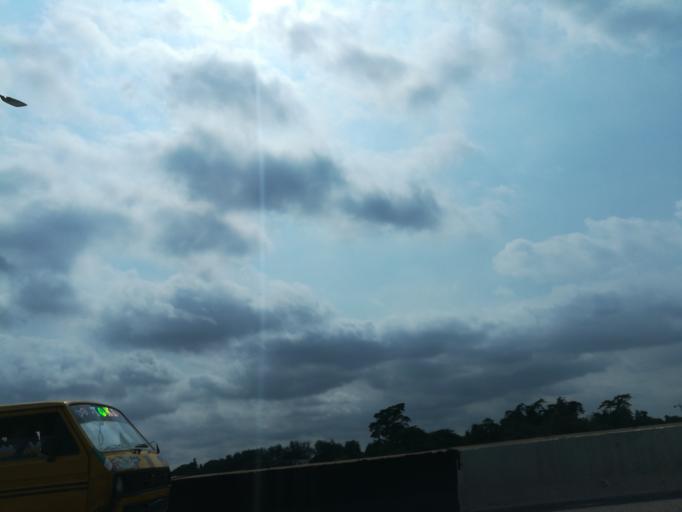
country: NG
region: Lagos
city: Makoko
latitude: 6.5136
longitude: 3.4055
